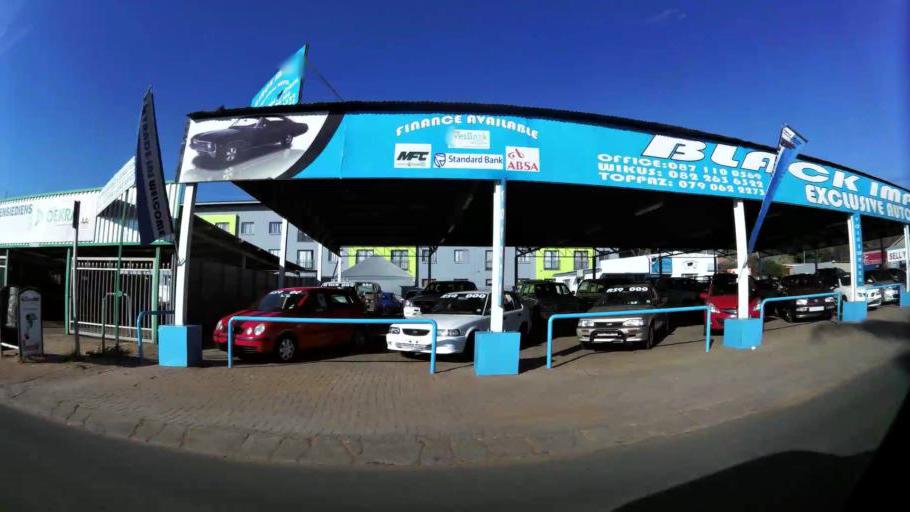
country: ZA
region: Gauteng
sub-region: City of Tshwane Metropolitan Municipality
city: Pretoria
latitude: -25.6771
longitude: 28.1663
